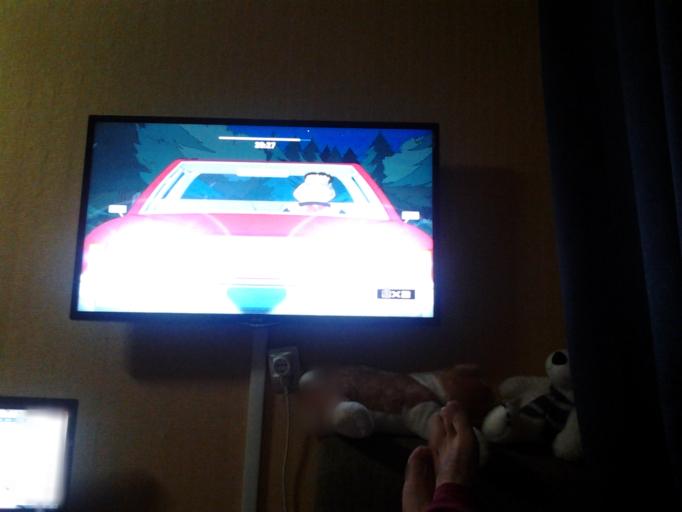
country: RU
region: Chelyabinsk
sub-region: Gorod Chelyabinsk
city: Chelyabinsk
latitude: 55.1820
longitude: 61.3348
